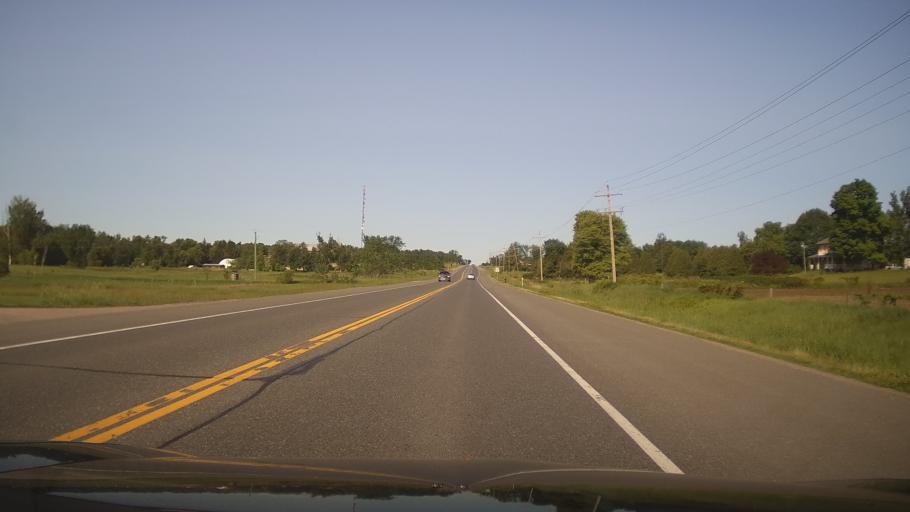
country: CA
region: Ontario
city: Peterborough
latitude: 44.3585
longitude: -78.0330
